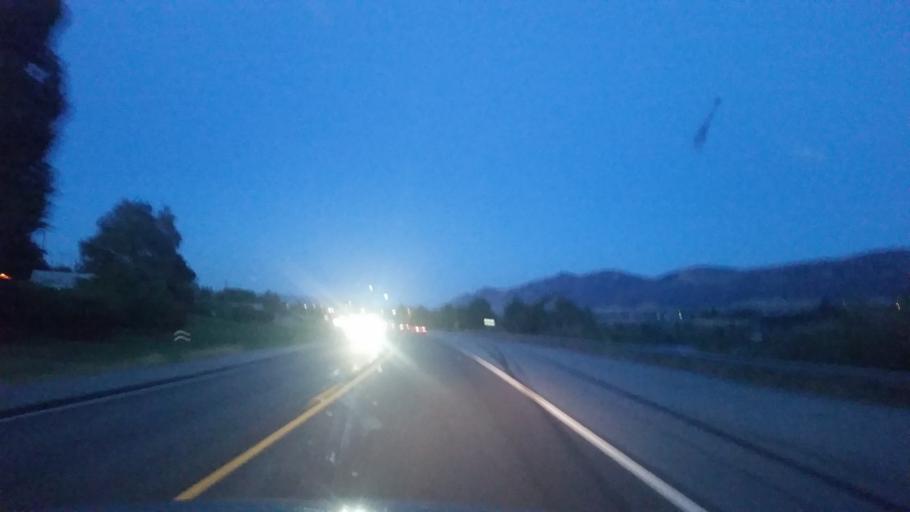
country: US
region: Washington
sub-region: Chelan County
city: South Wenatchee
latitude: 47.3858
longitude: -120.2586
